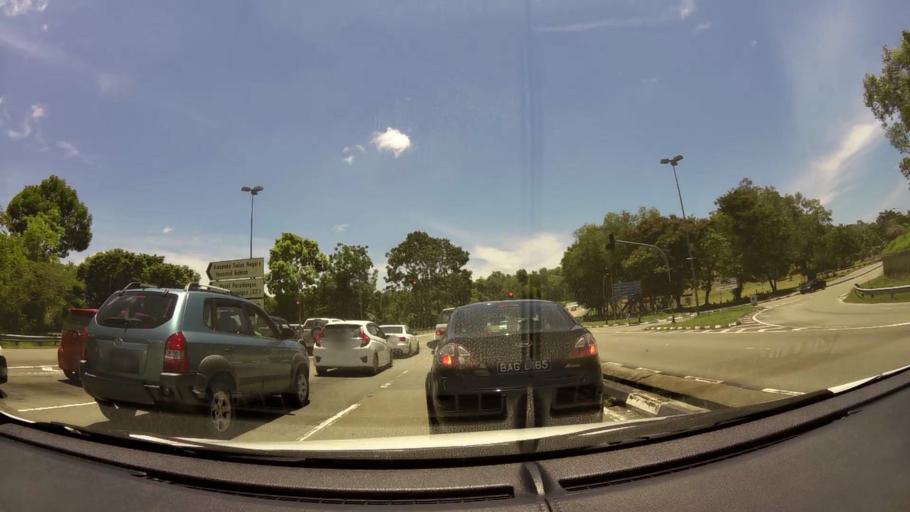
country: BN
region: Brunei and Muara
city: Bandar Seri Begawan
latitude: 4.9239
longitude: 114.9551
